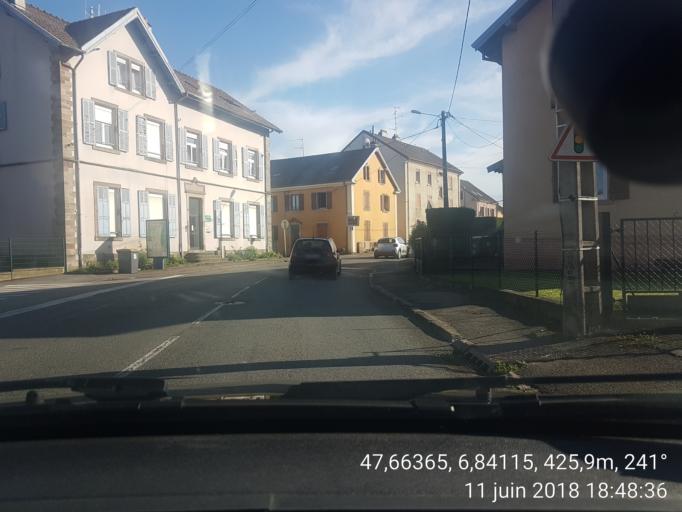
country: FR
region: Franche-Comte
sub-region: Territoire de Belfort
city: Valdoie
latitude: 47.6637
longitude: 6.8411
